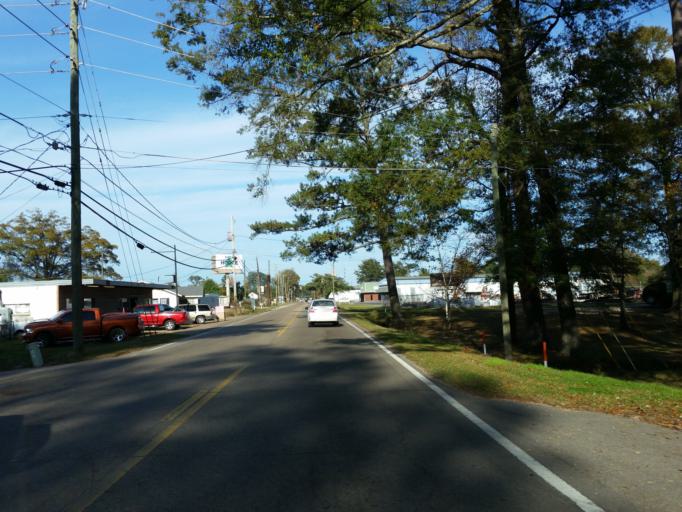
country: US
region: Mississippi
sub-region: Jones County
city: Laurel
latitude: 31.6564
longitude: -89.1672
